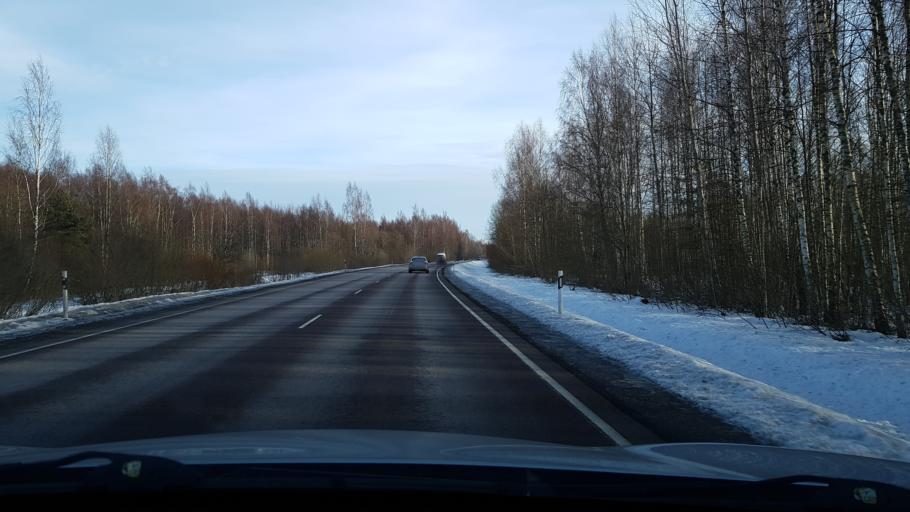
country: EE
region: Tartu
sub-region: Puhja vald
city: Puhja
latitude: 58.3958
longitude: 26.1163
